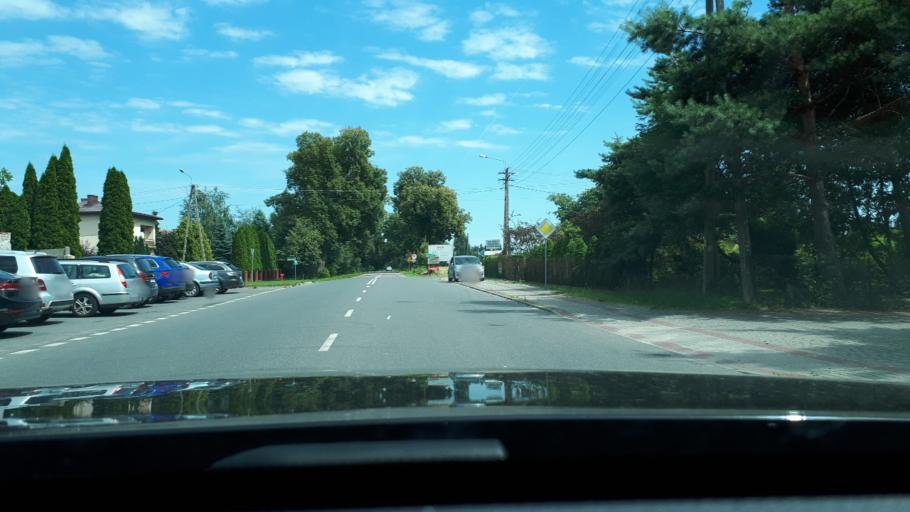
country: PL
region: Lodz Voivodeship
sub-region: powiat Lowicki
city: Nieborow
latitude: 52.0693
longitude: 20.0742
